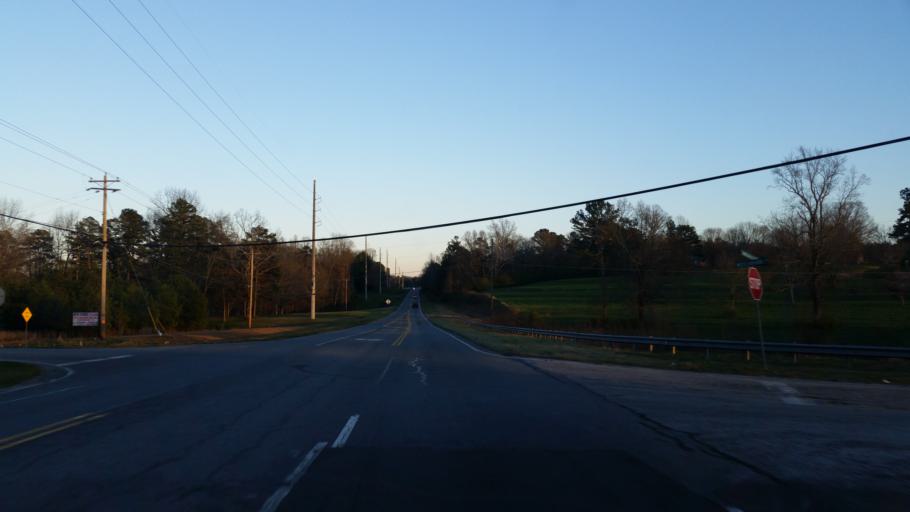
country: US
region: Georgia
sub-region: Hall County
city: Oakwood
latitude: 34.3111
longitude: -83.9926
